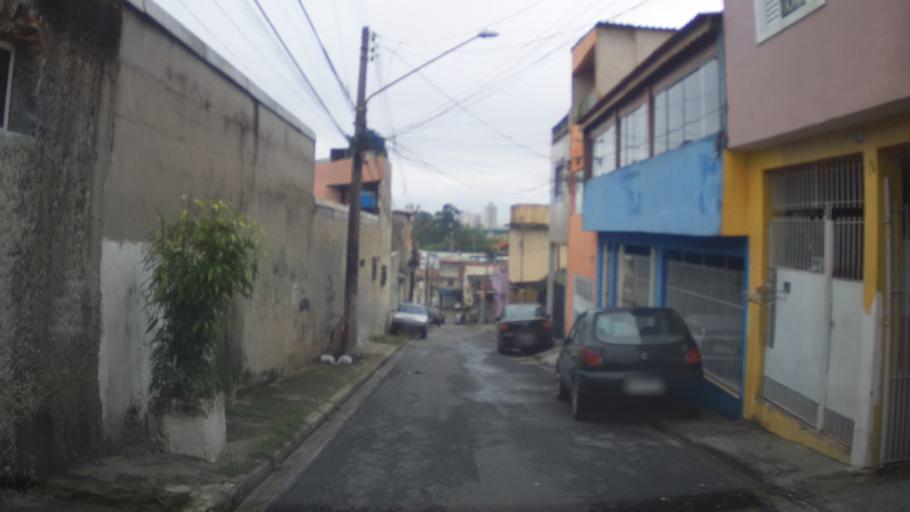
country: BR
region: Sao Paulo
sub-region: Guarulhos
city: Guarulhos
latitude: -23.5050
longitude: -46.5566
